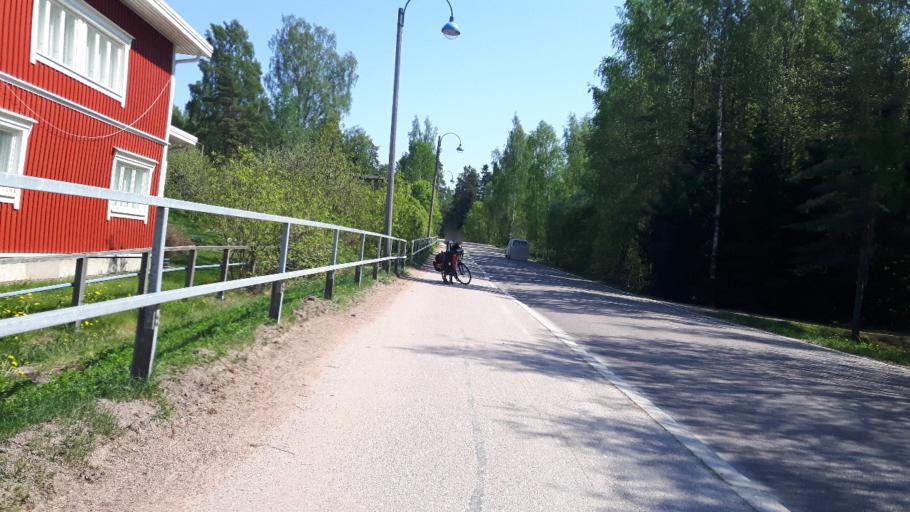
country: FI
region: Kymenlaakso
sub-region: Kotka-Hamina
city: Pyhtaeae
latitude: 60.4917
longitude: 26.5459
